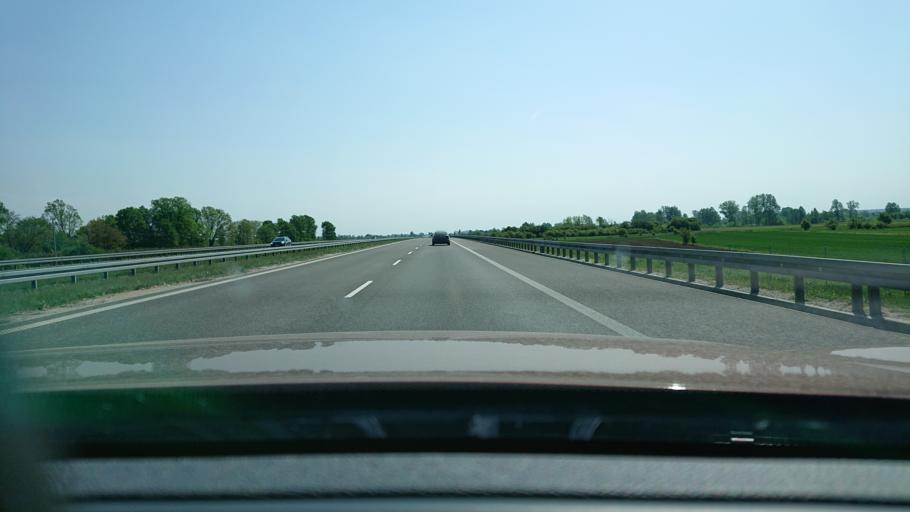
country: PL
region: Subcarpathian Voivodeship
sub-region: Powiat lancucki
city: Bialobrzegi
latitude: 50.1150
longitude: 22.3424
